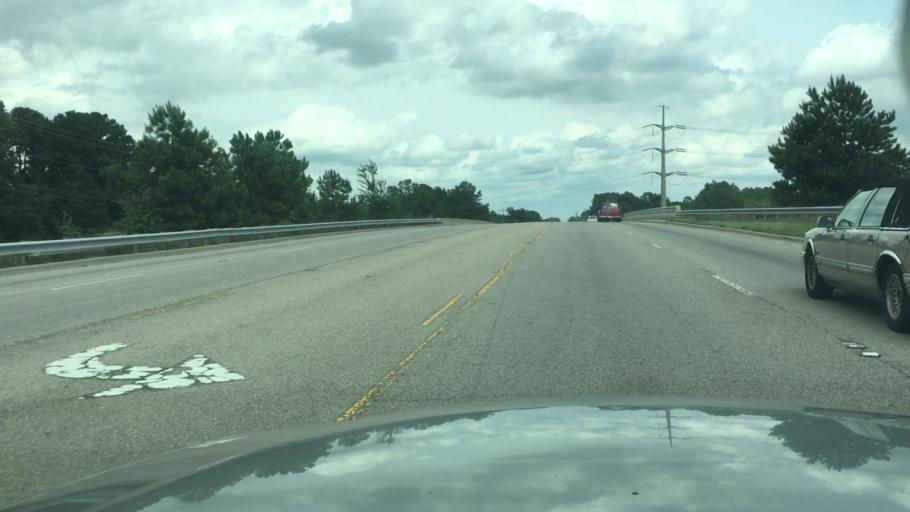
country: US
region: North Carolina
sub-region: Cumberland County
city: Hope Mills
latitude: 35.0168
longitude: -78.9245
